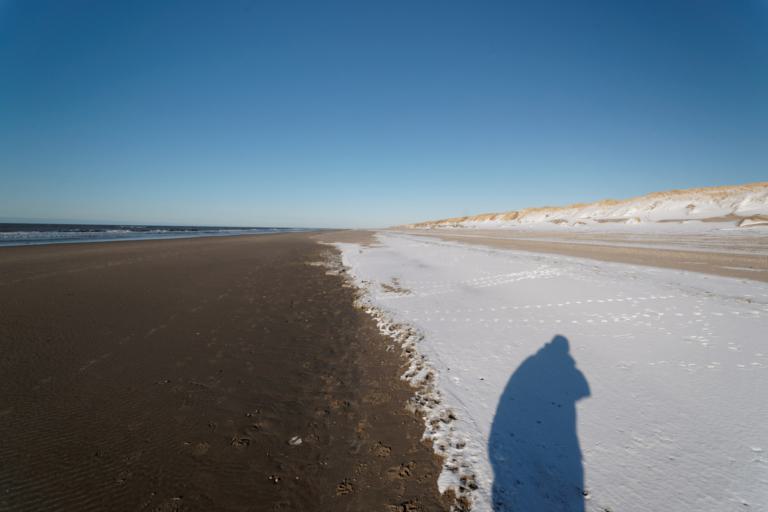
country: NL
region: North Holland
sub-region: Gemeente Texel
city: Den Burg
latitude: 53.1472
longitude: 4.8036
